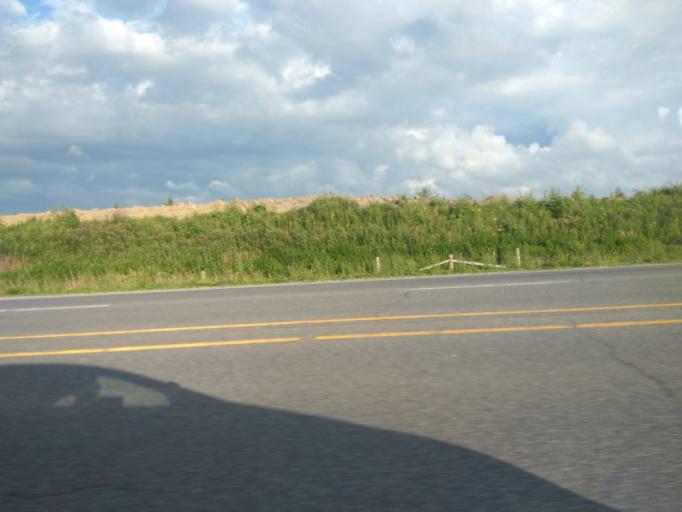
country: CA
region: Ontario
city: Kitchener
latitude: 43.3704
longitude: -80.7058
